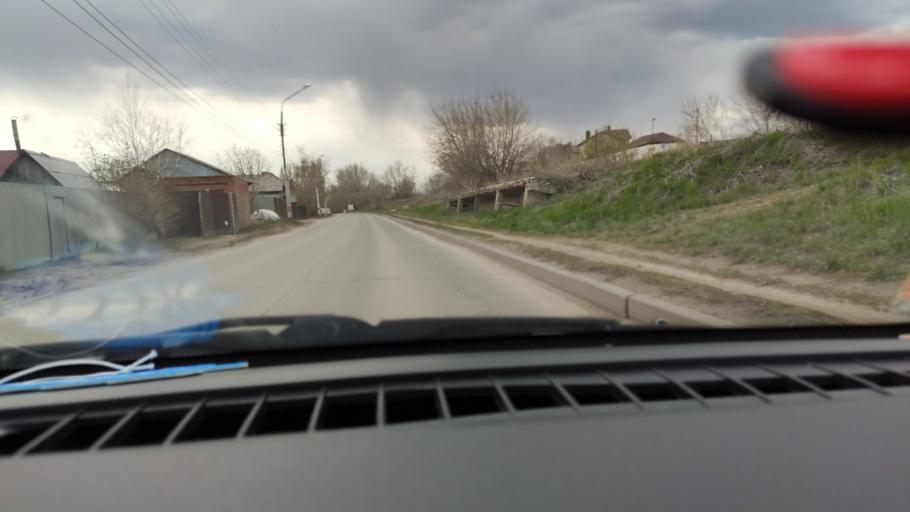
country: RU
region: Saratov
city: Engel's
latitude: 51.5005
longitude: 46.0651
